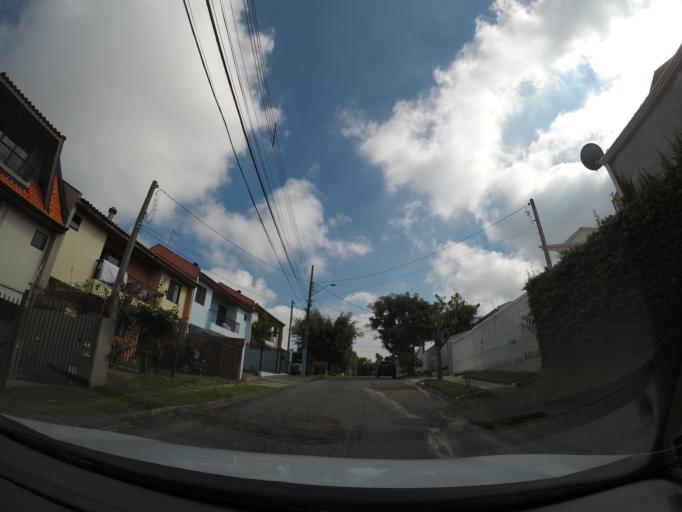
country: BR
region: Parana
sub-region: Sao Jose Dos Pinhais
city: Sao Jose dos Pinhais
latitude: -25.4904
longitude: -49.2181
